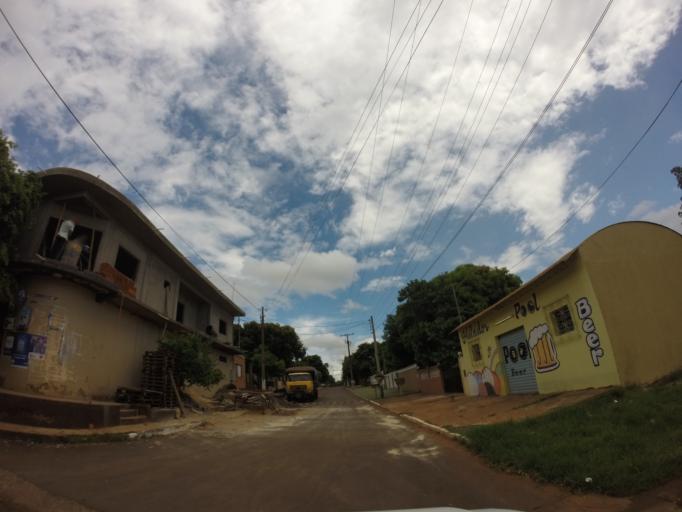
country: PY
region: Alto Parana
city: Ciudad del Este
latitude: -25.4162
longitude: -54.6304
